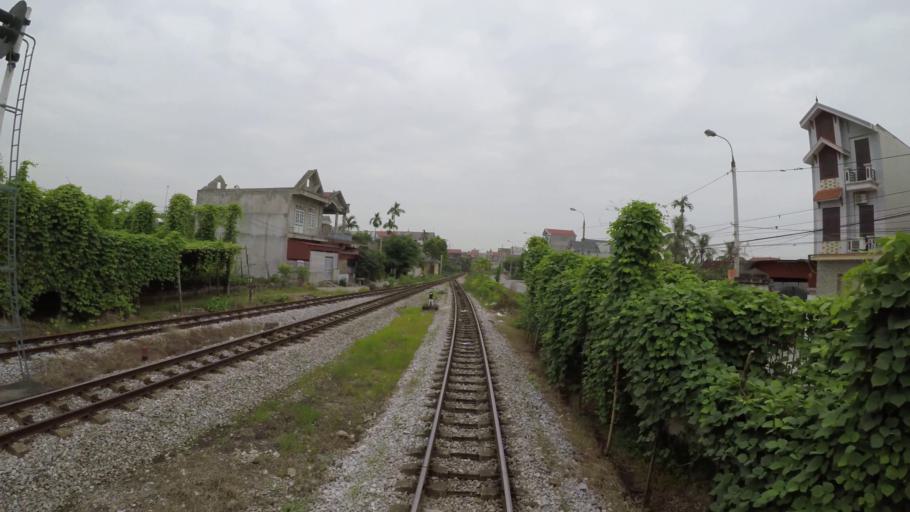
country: VN
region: Hai Duong
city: Phu Thai
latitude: 20.9688
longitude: 106.5004
